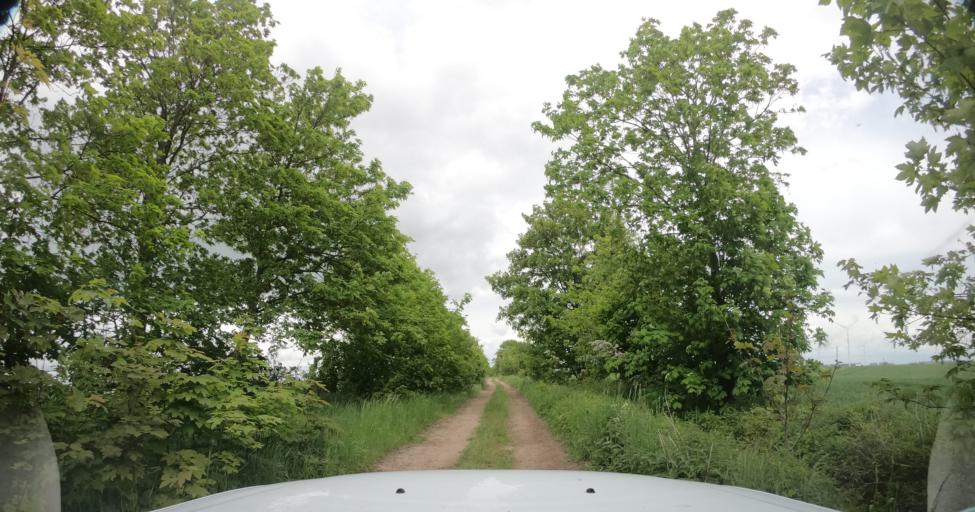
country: PL
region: West Pomeranian Voivodeship
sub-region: Powiat pyrzycki
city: Kozielice
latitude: 53.0850
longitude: 14.8251
